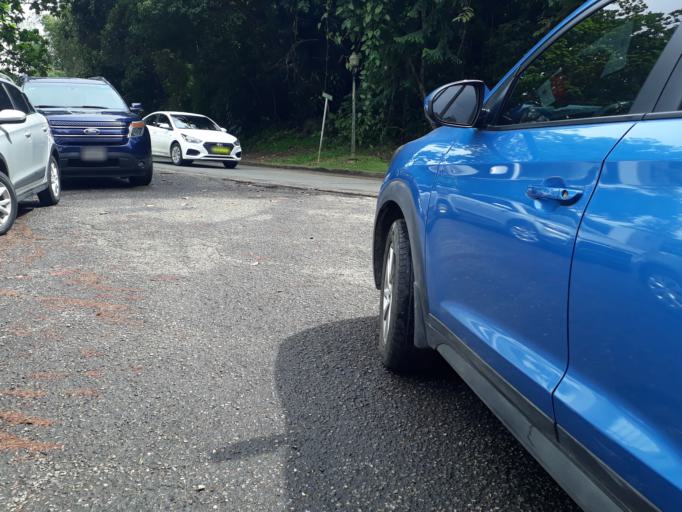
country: PA
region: Panama
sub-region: Distrito de Panama
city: Ancon
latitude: 8.9623
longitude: -79.5504
